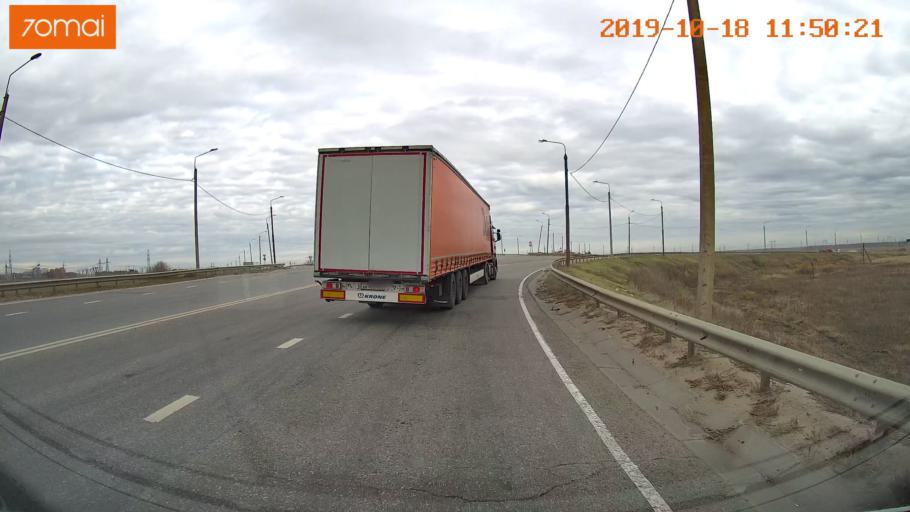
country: RU
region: Rjazan
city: Mikhaylov
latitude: 54.2602
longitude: 39.0026
